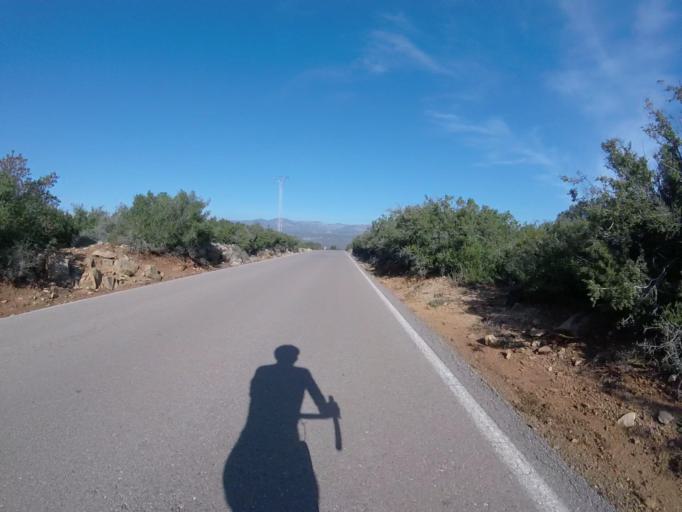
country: ES
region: Valencia
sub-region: Provincia de Castello
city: Benlloch
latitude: 40.2381
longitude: 0.0724
